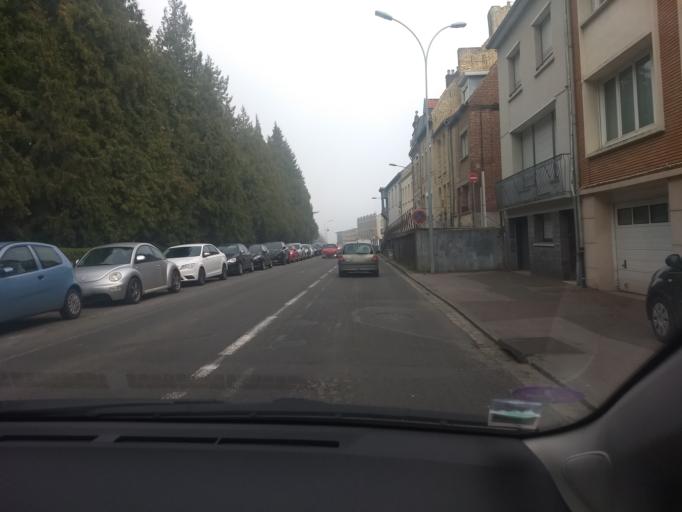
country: FR
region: Nord-Pas-de-Calais
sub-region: Departement du Pas-de-Calais
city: Saint-Omer
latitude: 50.7490
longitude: 2.2501
